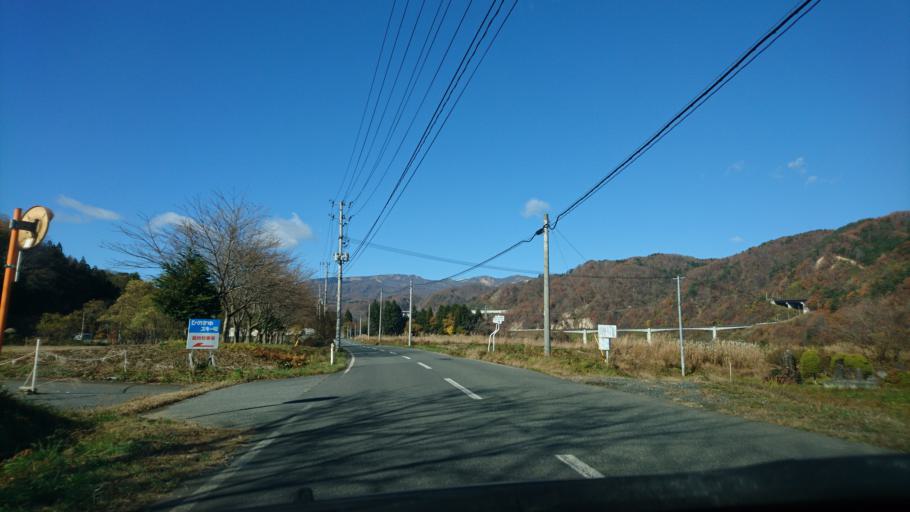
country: JP
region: Iwate
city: Mizusawa
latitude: 39.1175
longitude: 140.9409
